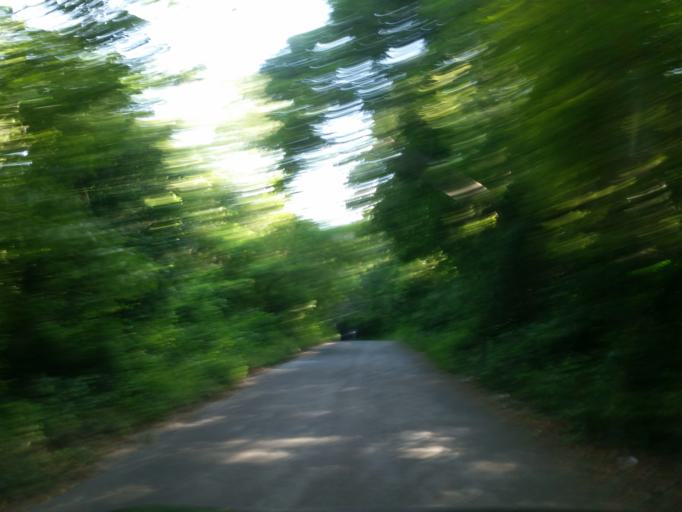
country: NI
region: Masaya
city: Catarina
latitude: 11.9310
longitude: -86.0564
